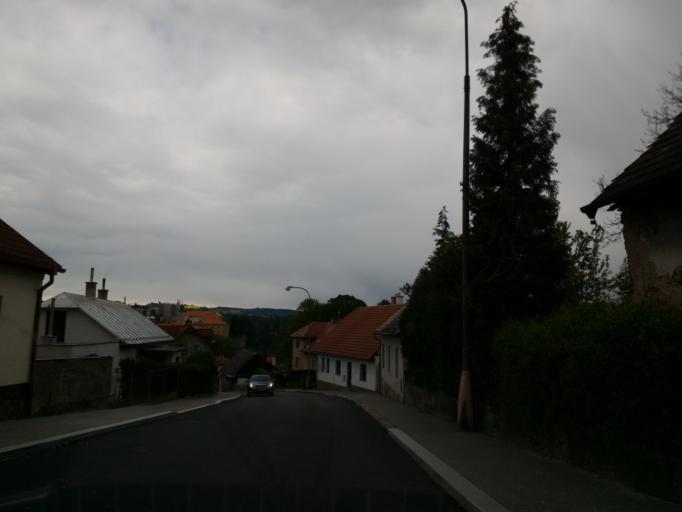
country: CZ
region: Vysocina
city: Ledec nad Sazavou
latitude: 49.6916
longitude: 15.2823
